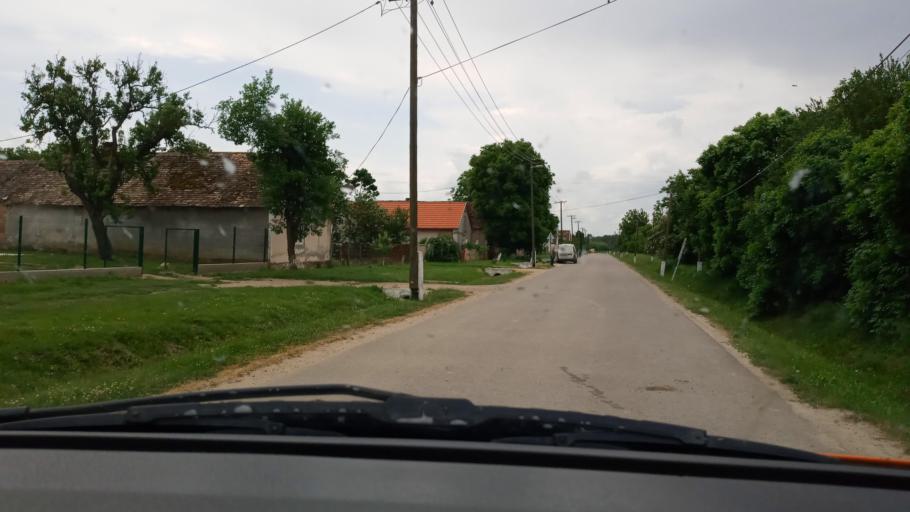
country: HU
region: Baranya
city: Vajszlo
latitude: 45.8267
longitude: 17.9942
